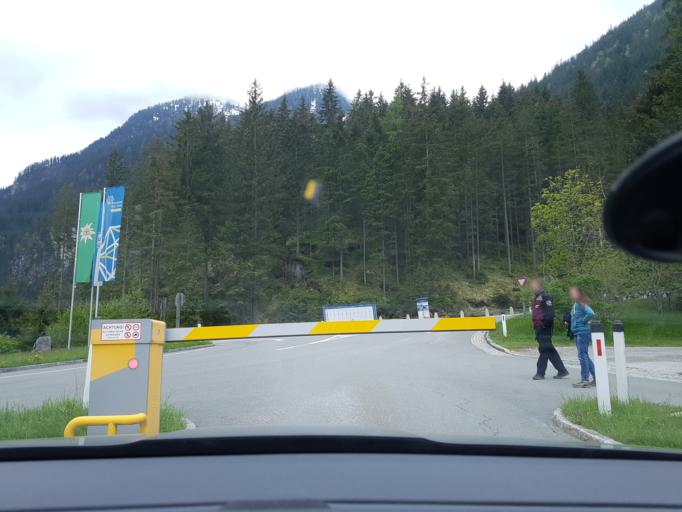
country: AT
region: Salzburg
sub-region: Politischer Bezirk Zell am See
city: Krimml
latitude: 47.2139
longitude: 12.1680
